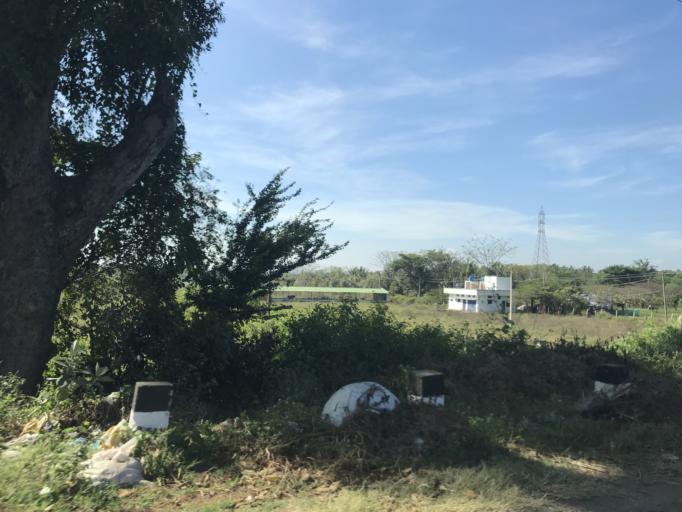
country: IN
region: Karnataka
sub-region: Mysore
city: Heggadadevankote
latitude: 12.1217
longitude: 76.4763
